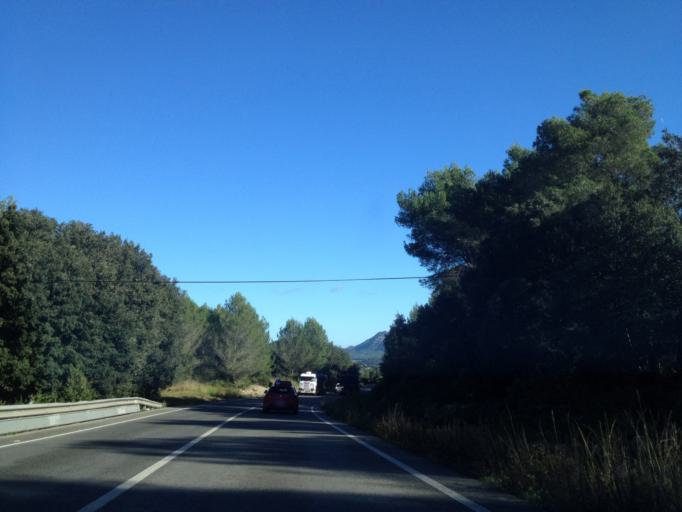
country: ES
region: Balearic Islands
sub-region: Illes Balears
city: Arta
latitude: 39.6781
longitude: 3.3364
